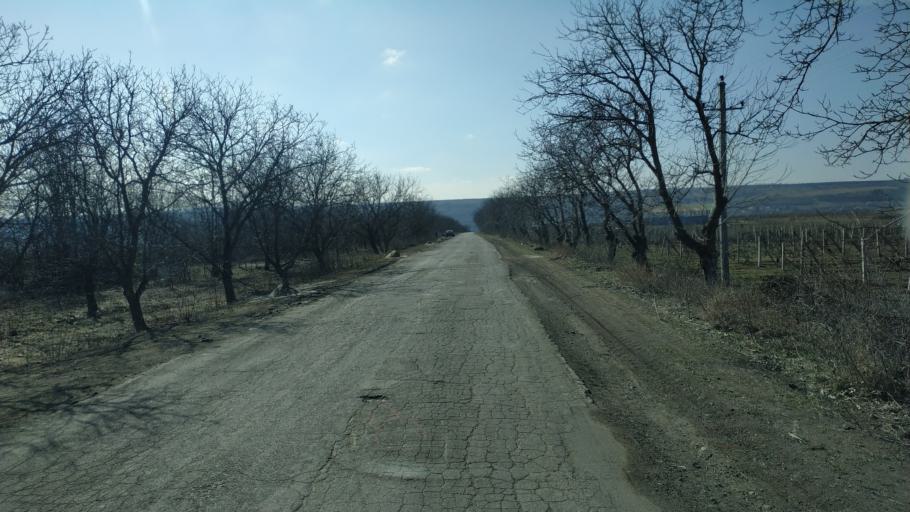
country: MD
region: Hincesti
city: Hincesti
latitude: 46.7612
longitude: 28.6666
